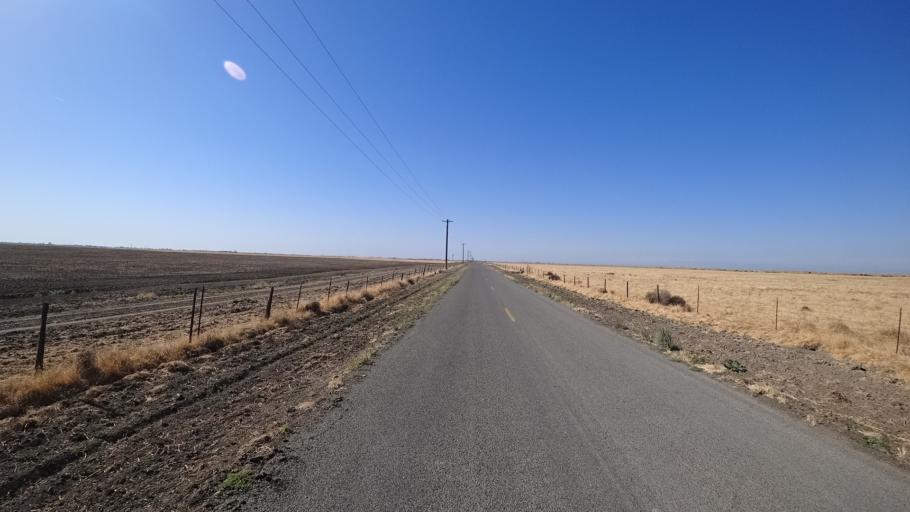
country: US
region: California
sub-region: Kings County
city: Corcoran
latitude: 36.1764
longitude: -119.5649
